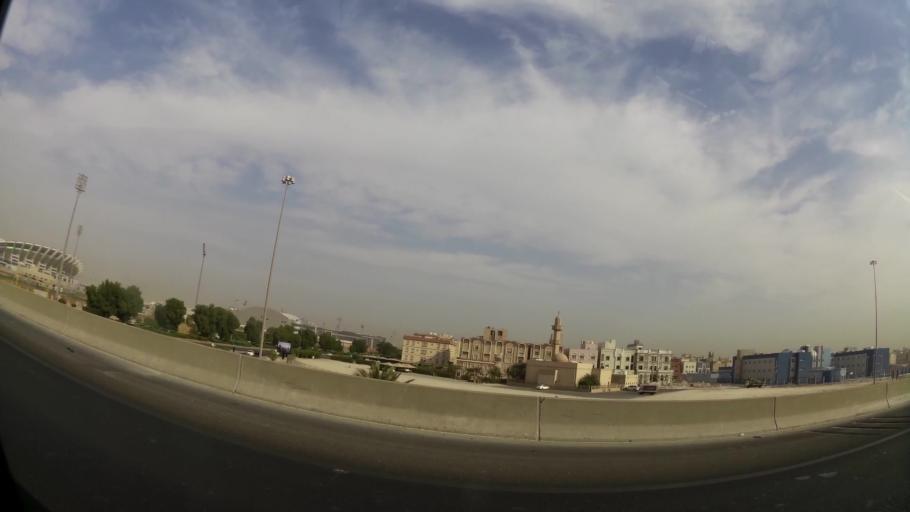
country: KW
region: Al Asimah
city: Ar Rabiyah
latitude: 29.2671
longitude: 47.9262
